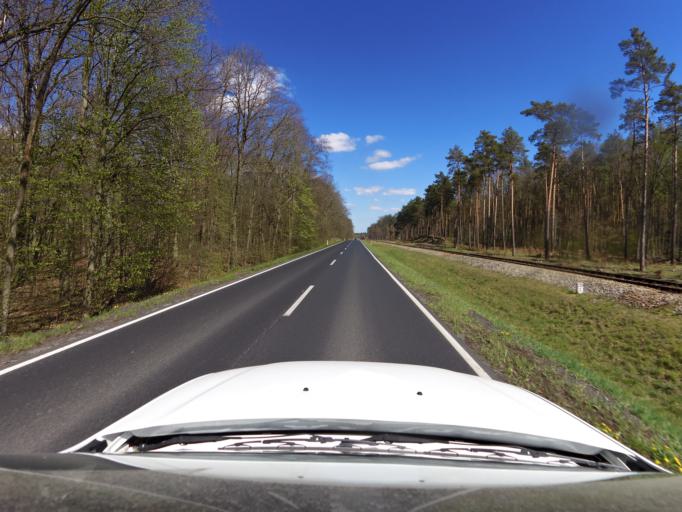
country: PL
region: West Pomeranian Voivodeship
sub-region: Powiat mysliborski
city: Debno
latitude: 52.7513
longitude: 14.7259
